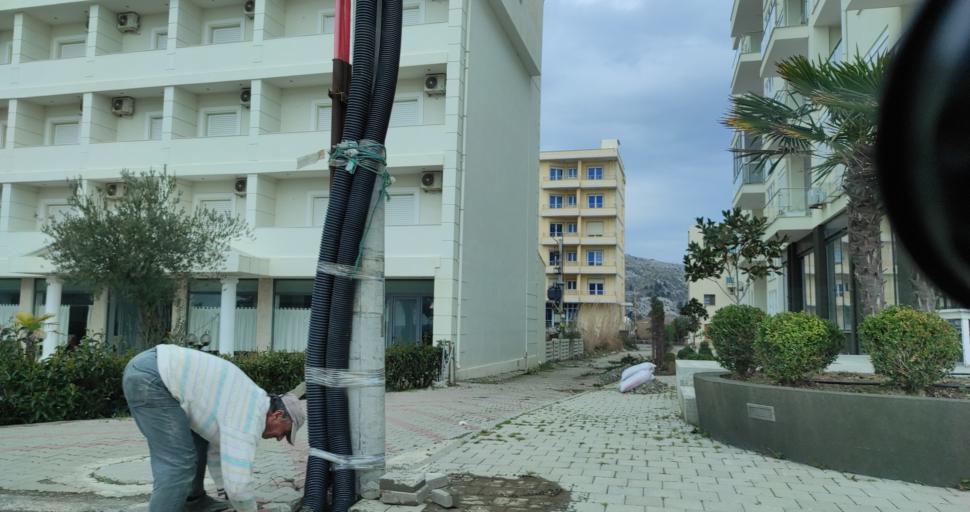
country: AL
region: Lezhe
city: Shengjin
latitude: 41.7968
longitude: 19.6019
